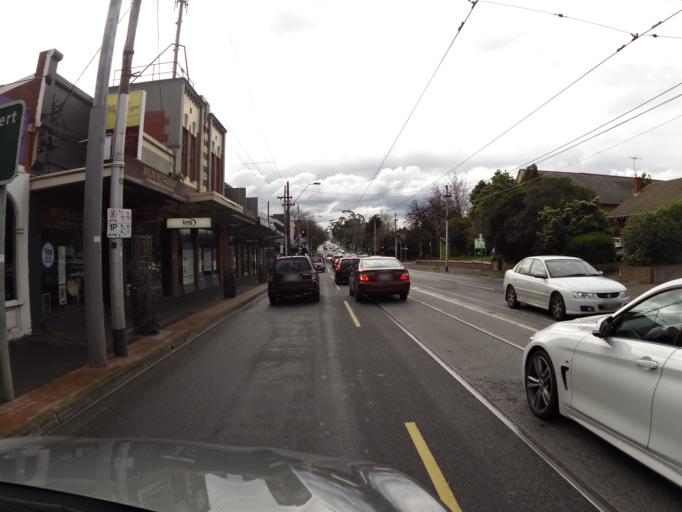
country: AU
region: Victoria
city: Balwyn
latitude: -37.8166
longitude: 145.0594
